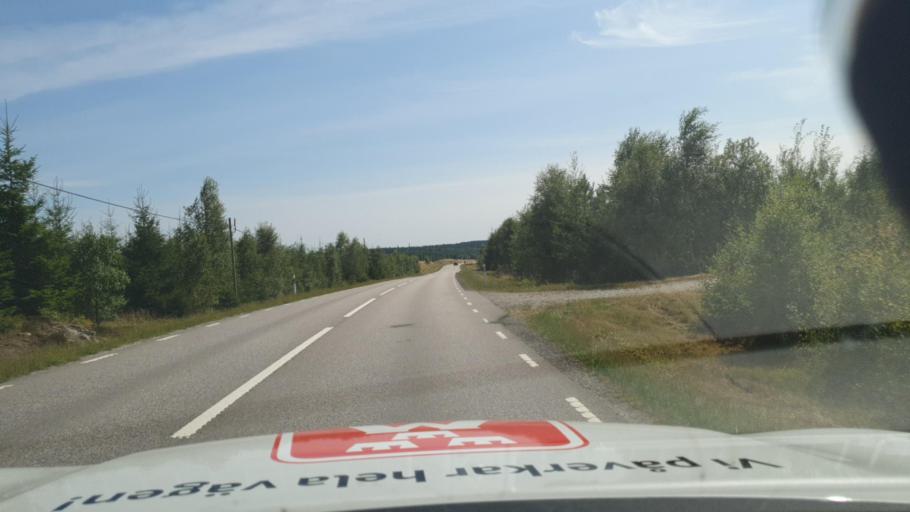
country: SE
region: Vaestra Goetaland
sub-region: Essunga Kommun
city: Nossebro
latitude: 58.1047
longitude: 12.6534
